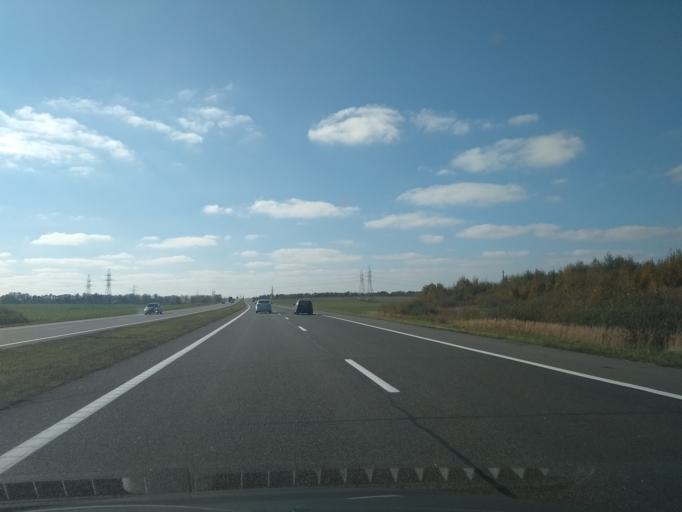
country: BY
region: Brest
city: Baranovichi
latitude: 53.1737
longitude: 26.0057
